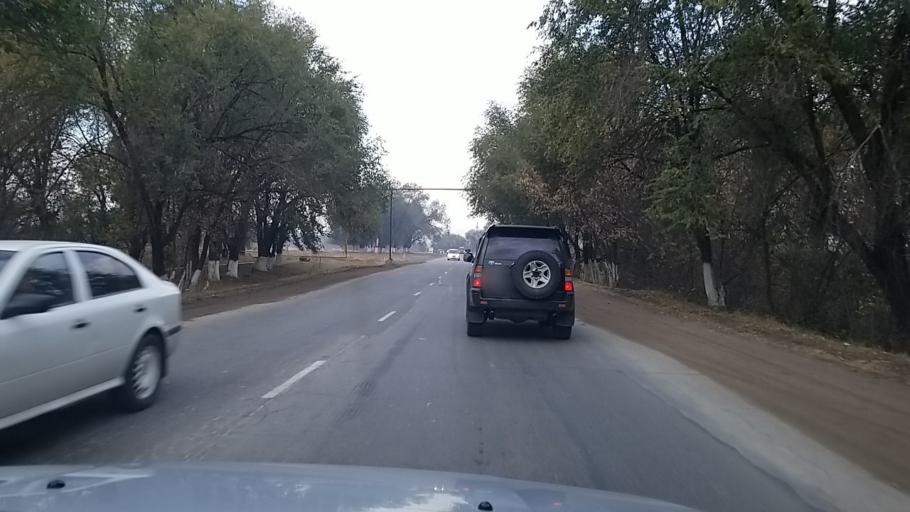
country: KZ
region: Almaty Oblysy
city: Burunday
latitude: 43.3599
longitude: 76.7513
